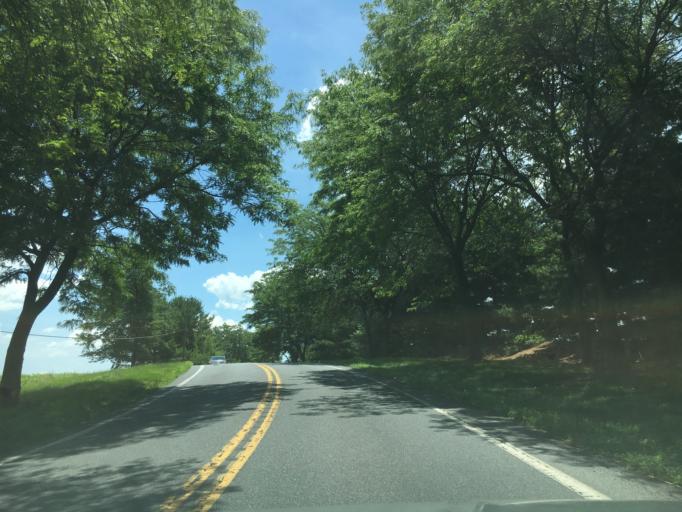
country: US
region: Pennsylvania
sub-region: Lehigh County
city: Schnecksville
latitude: 40.6591
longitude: -75.5762
